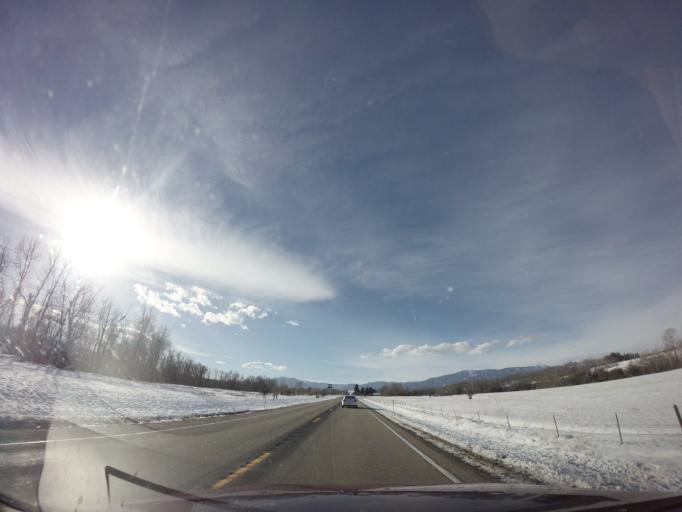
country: US
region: Montana
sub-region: Carbon County
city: Red Lodge
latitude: 45.2823
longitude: -109.2143
